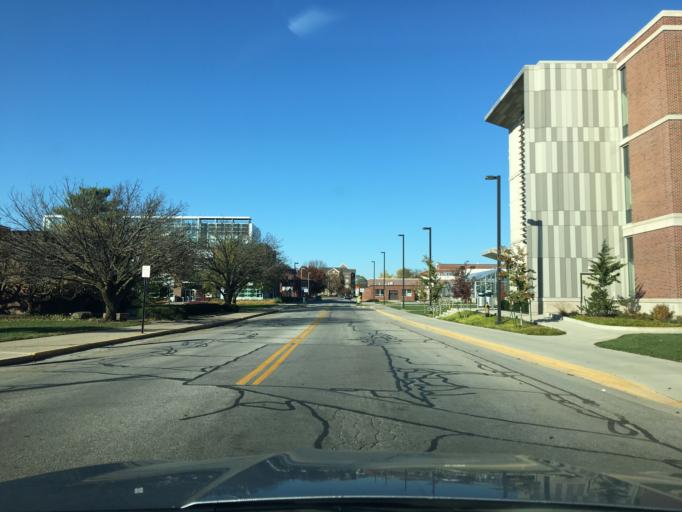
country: US
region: Indiana
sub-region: Tippecanoe County
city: West Lafayette
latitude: 40.4210
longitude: -86.9194
